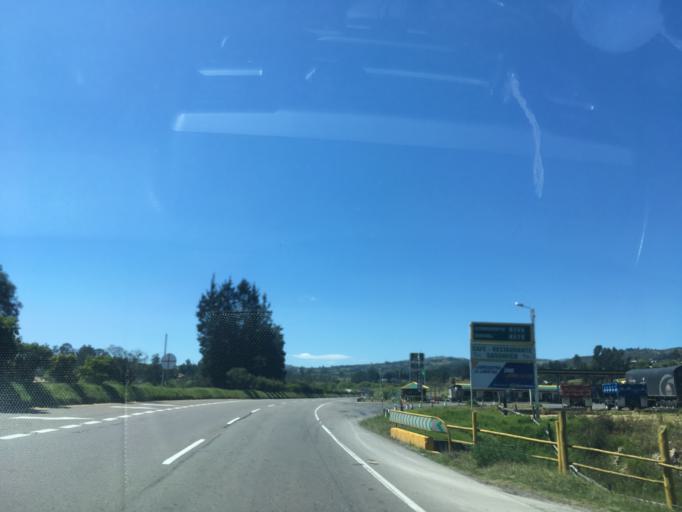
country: CO
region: Boyaca
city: Tuta
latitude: 5.7113
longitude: -73.2397
